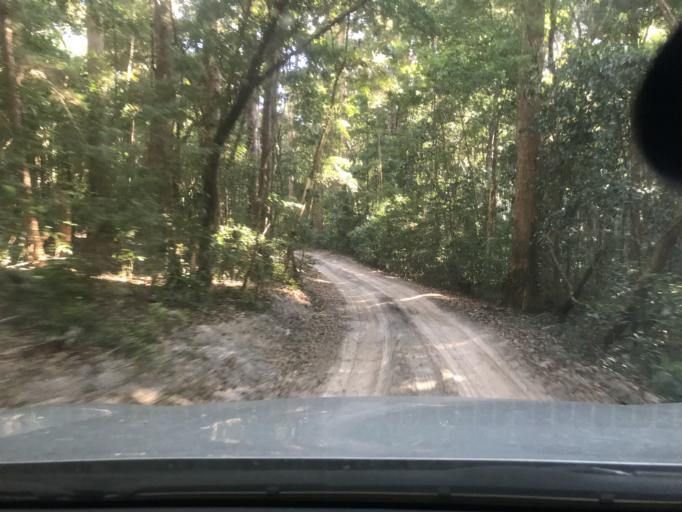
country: AU
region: Queensland
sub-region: Fraser Coast
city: Urangan
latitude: -25.3246
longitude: 153.1520
